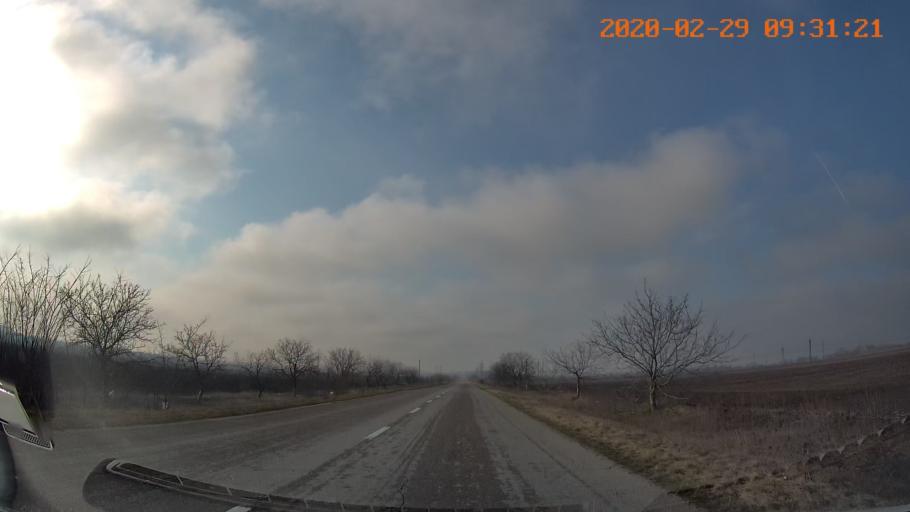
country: MD
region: Telenesti
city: Dnestrovsc
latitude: 46.6541
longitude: 29.9117
